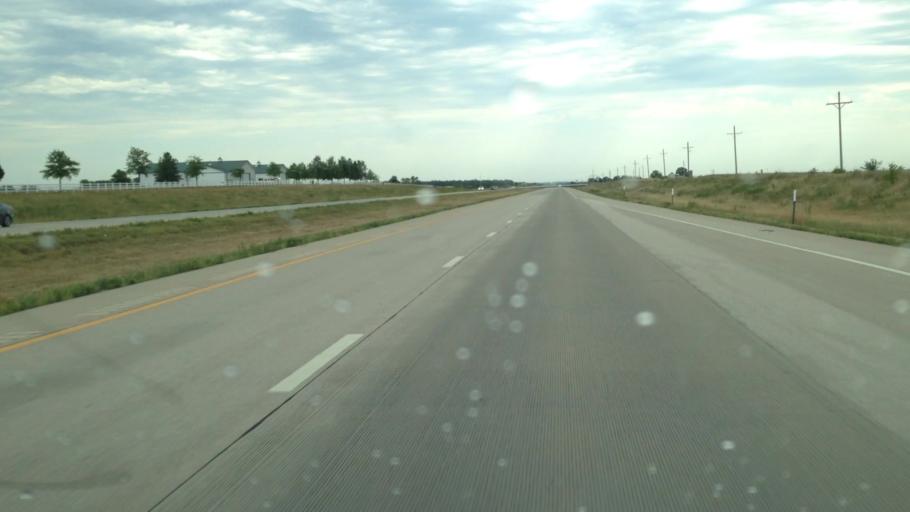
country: US
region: Kansas
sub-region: Douglas County
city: Baldwin City
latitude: 38.8294
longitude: -95.2695
